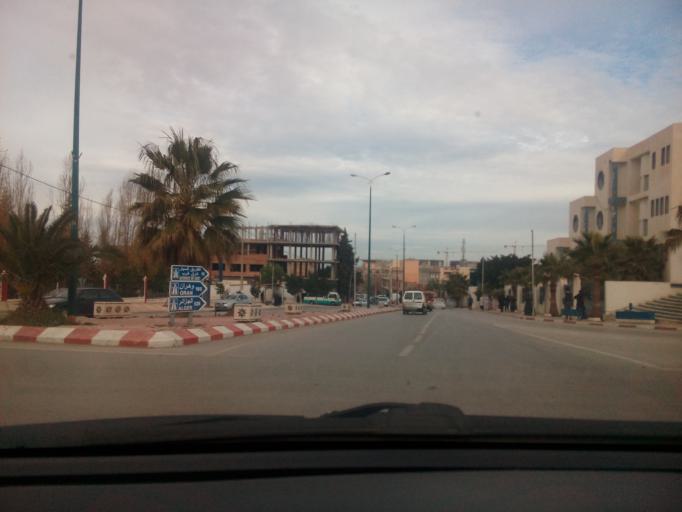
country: DZ
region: Tlemcen
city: Mansoura
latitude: 34.8789
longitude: -1.3486
